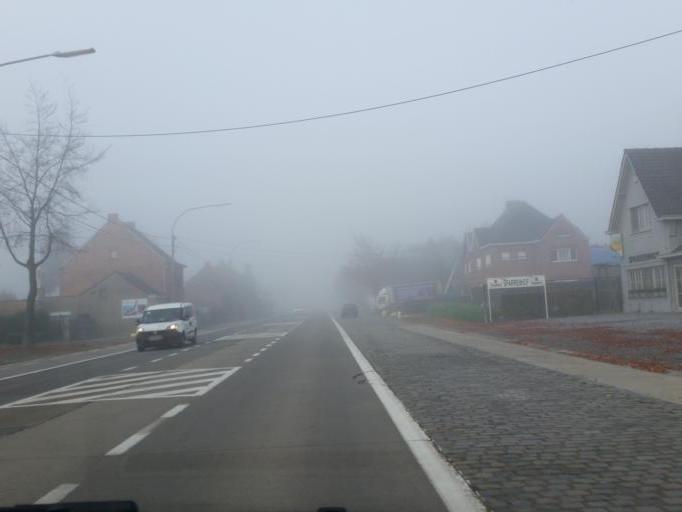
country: BE
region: Flanders
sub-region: Provincie Oost-Vlaanderen
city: Lede
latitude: 50.9477
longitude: 3.9496
